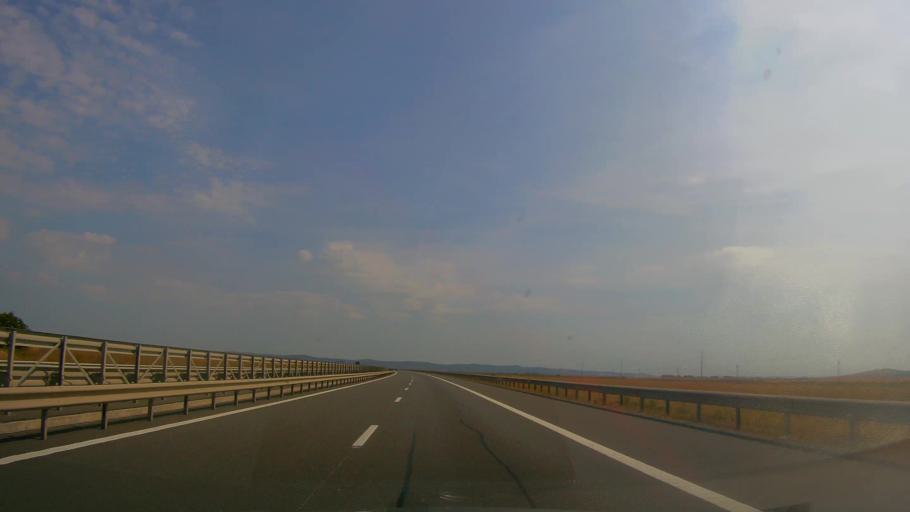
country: RO
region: Cluj
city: Turda
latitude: 46.5233
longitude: 23.8162
